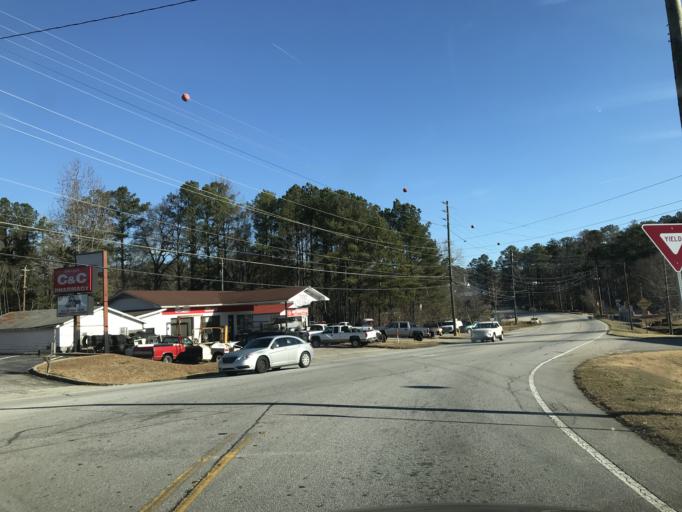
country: US
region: Georgia
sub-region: Paulding County
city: Dallas
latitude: 33.9203
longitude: -84.8533
